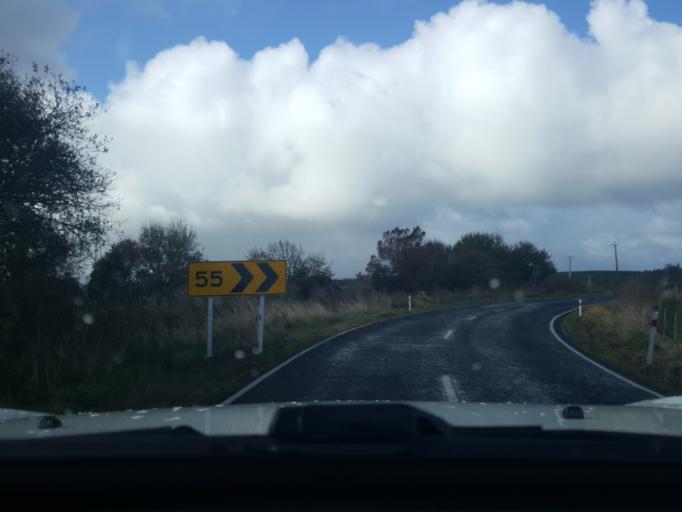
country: NZ
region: Waikato
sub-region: Waikato District
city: Te Kauwhata
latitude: -37.4479
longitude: 175.0939
